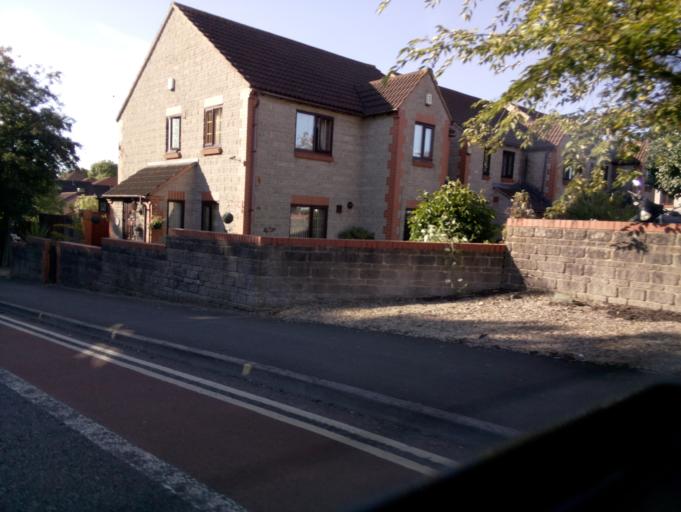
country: GB
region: England
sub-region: South Gloucestershire
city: Kingswood
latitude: 51.4513
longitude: -2.5212
